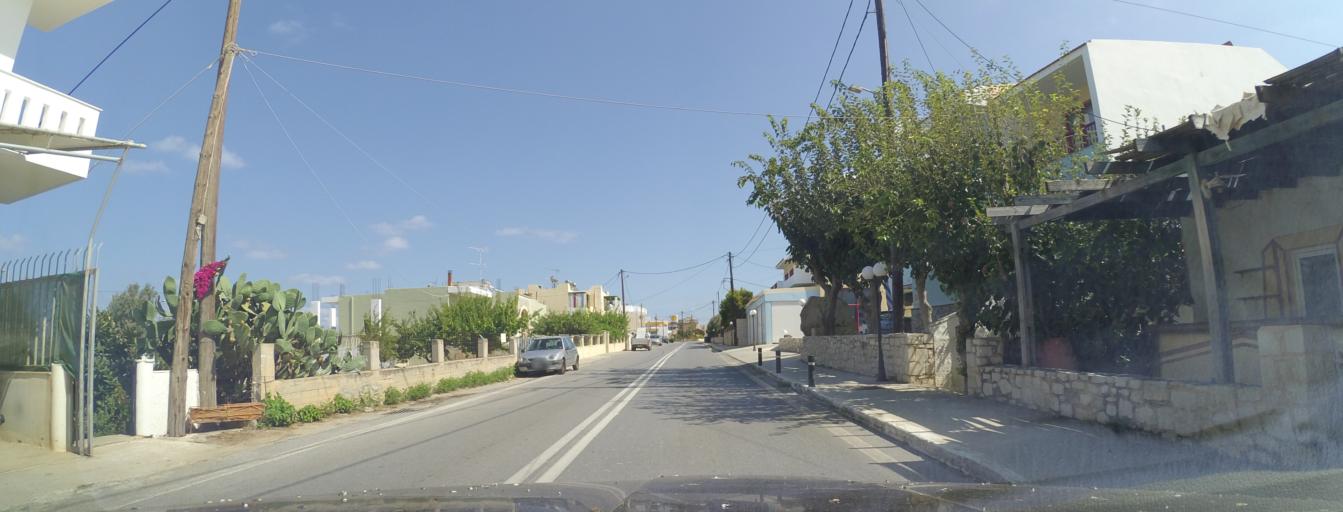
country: GR
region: Crete
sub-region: Nomos Rethymnis
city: Panormos
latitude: 35.3831
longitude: 24.5906
